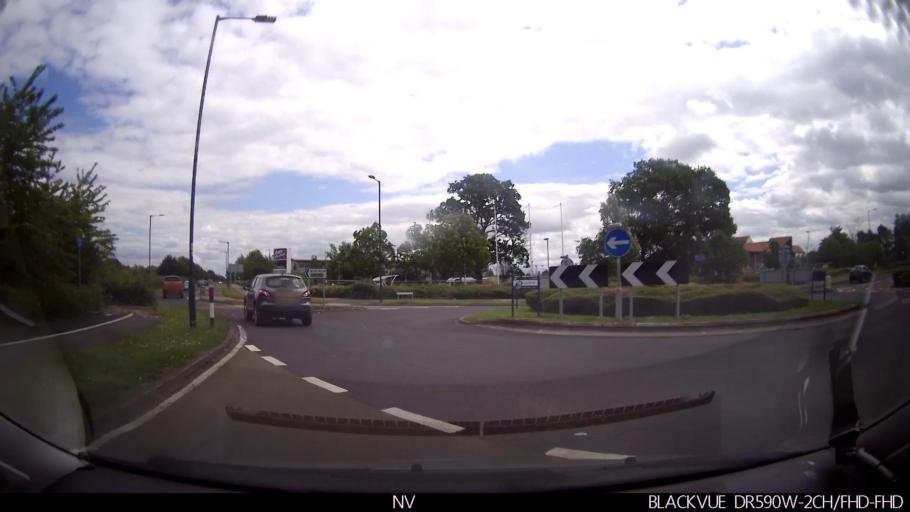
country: GB
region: England
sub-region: City of York
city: Wigginton
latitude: 53.9950
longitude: -1.0965
